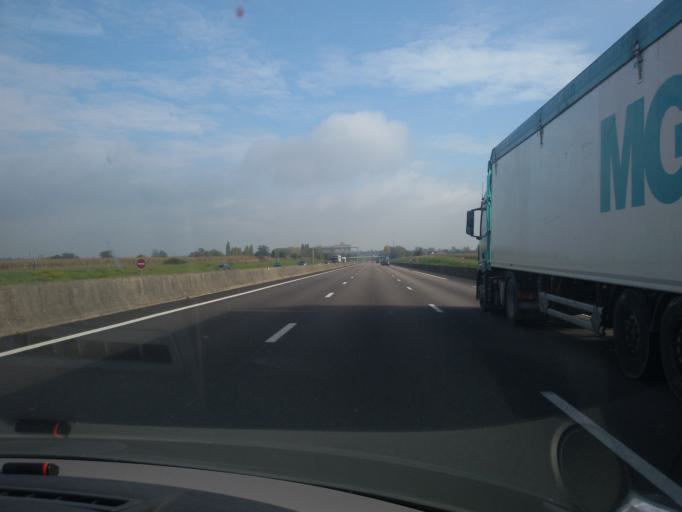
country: FR
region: Haute-Normandie
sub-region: Departement de l'Eure
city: Bourg-Achard
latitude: 49.3639
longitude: 0.8317
